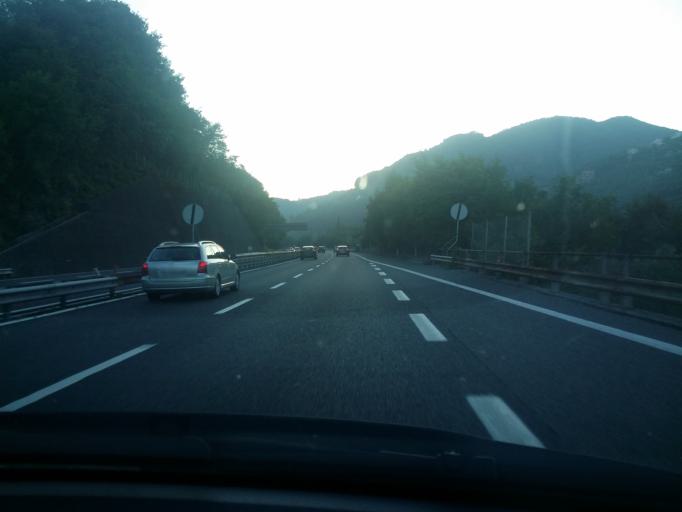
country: IT
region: Liguria
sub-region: Provincia di Genova
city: Chiavari
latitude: 44.3299
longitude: 9.3132
